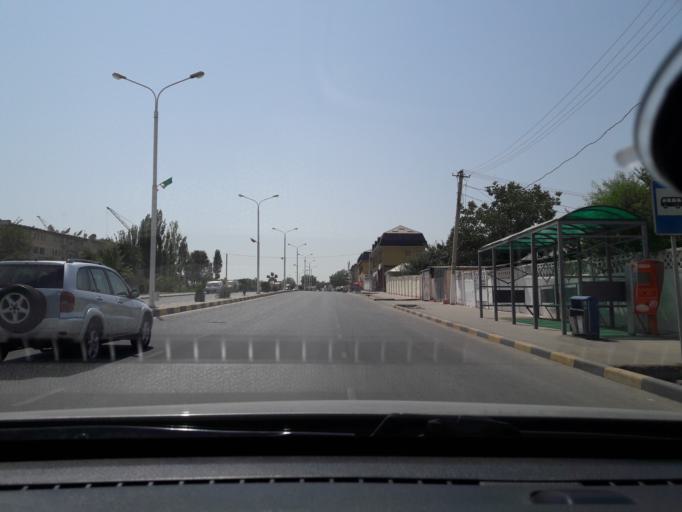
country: TJ
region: Dushanbe
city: Dushanbe
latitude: 38.5844
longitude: 68.7083
